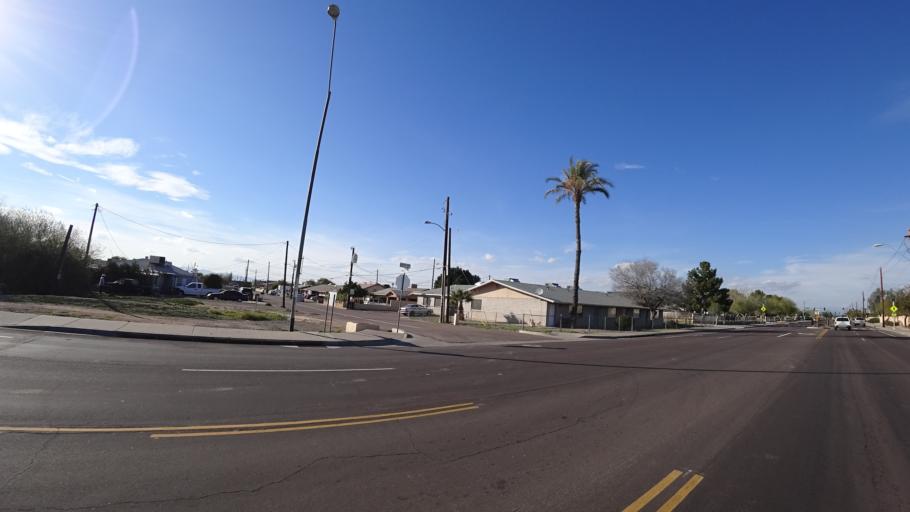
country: US
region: Arizona
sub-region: Maricopa County
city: Peoria
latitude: 33.5842
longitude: -112.2377
